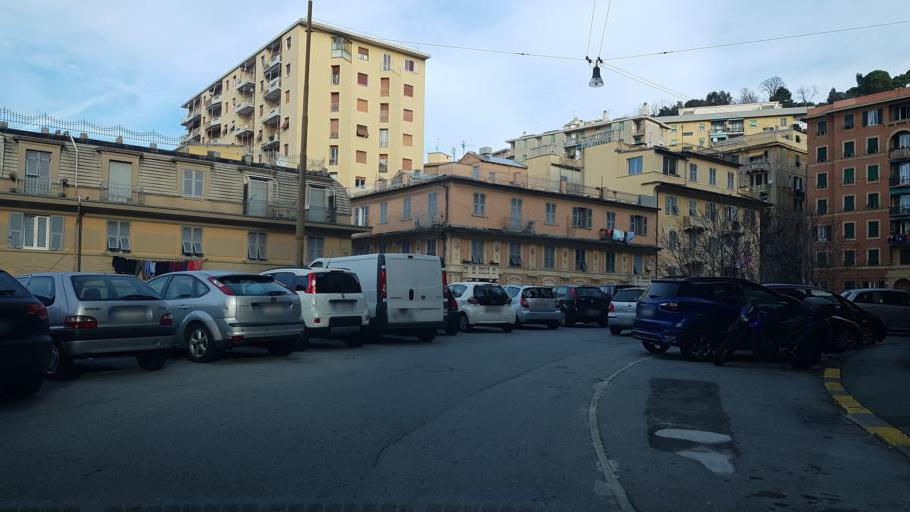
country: IT
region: Liguria
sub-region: Provincia di Genova
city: San Teodoro
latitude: 44.4150
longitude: 8.8916
